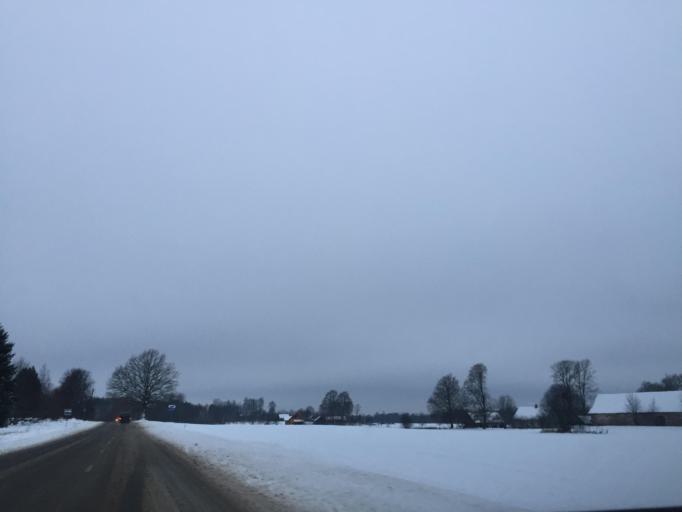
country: LV
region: Smiltene
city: Smiltene
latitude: 57.4367
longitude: 25.7719
